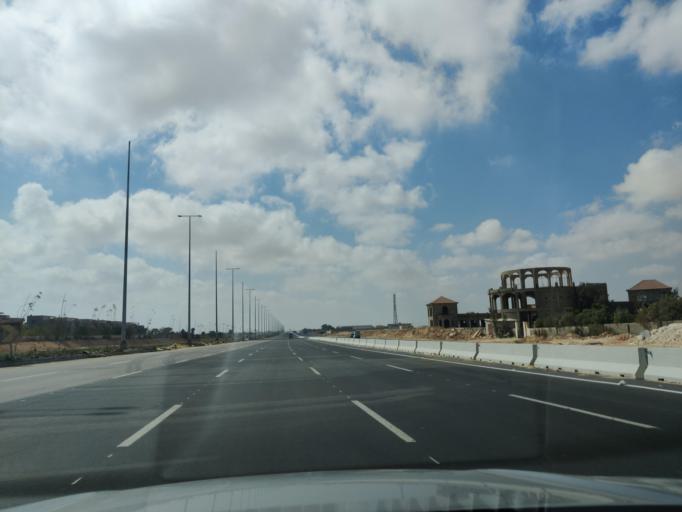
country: EG
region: Muhafazat Matruh
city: Al `Alamayn
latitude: 30.9393
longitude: 28.7840
